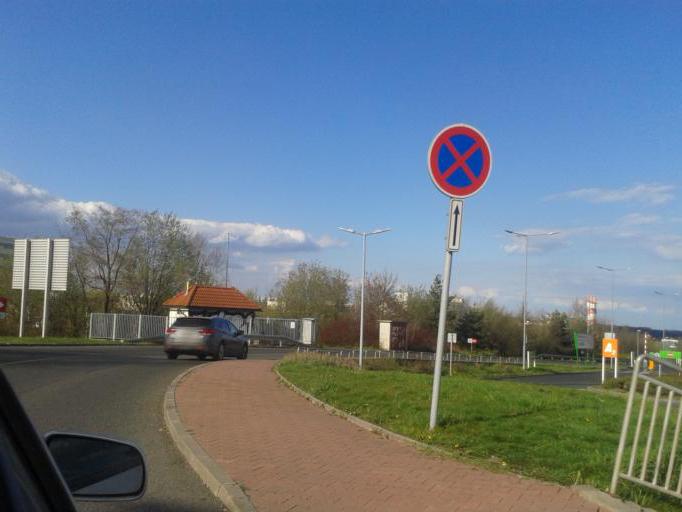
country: CZ
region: Central Bohemia
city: Hostivice
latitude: 50.0527
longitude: 14.2932
